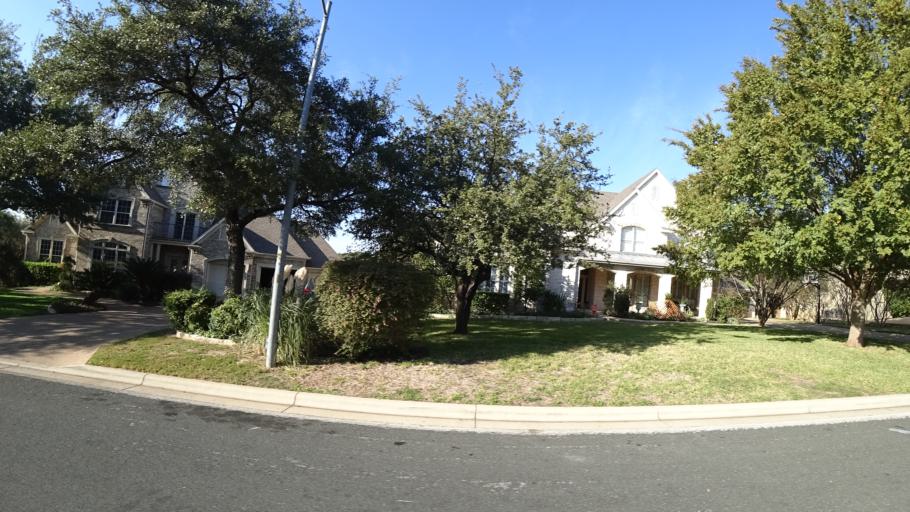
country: US
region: Texas
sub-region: Williamson County
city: Anderson Mill
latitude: 30.4383
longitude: -97.8127
